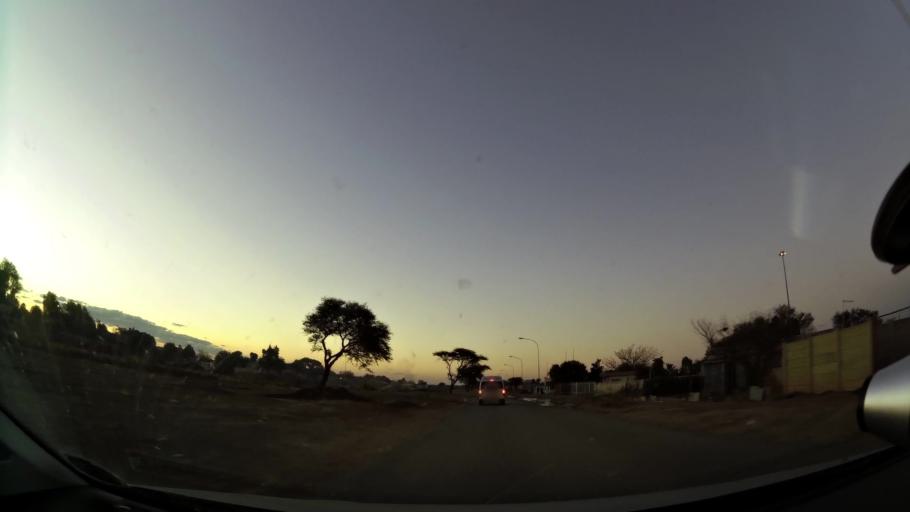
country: ZA
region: Northern Cape
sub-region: Frances Baard District Municipality
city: Kimberley
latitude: -28.7187
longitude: 24.7629
